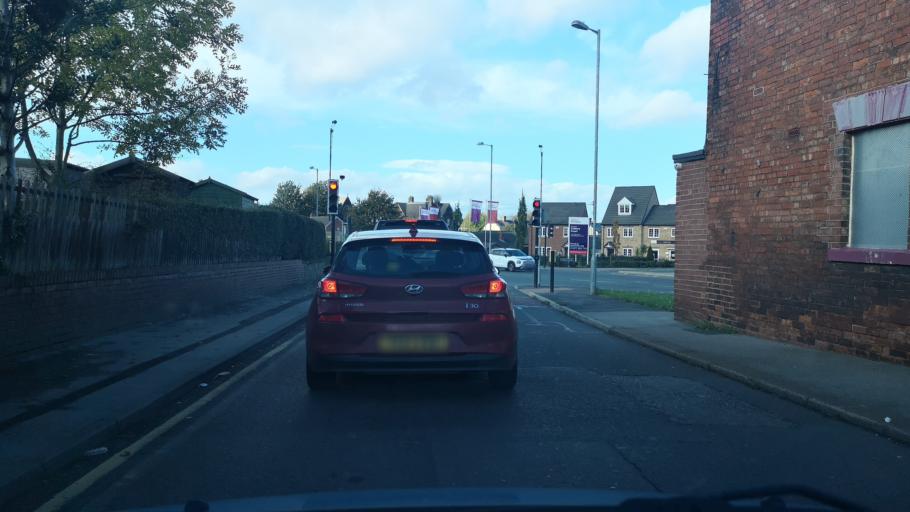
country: GB
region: England
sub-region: City and Borough of Wakefield
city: Featherstone
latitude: 53.6742
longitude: -1.3532
